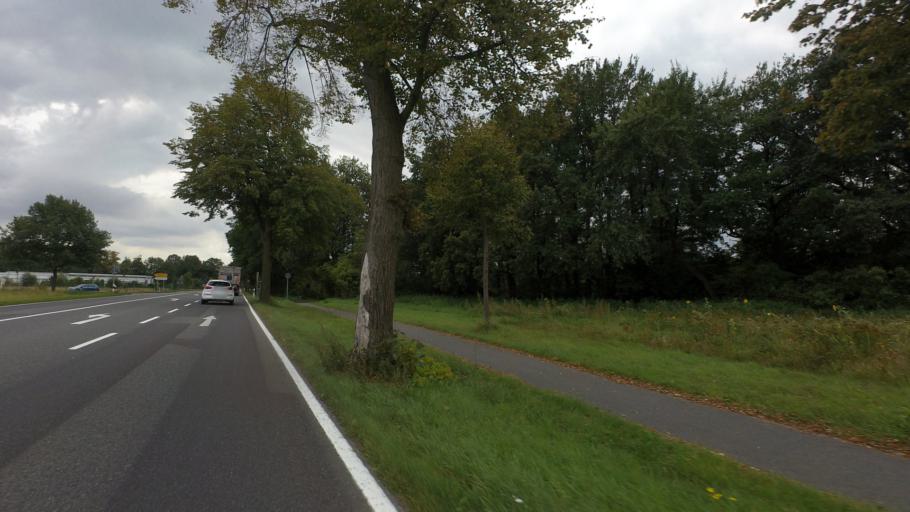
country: DE
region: Saxony
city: Neschwitz
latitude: 51.2721
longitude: 14.3423
